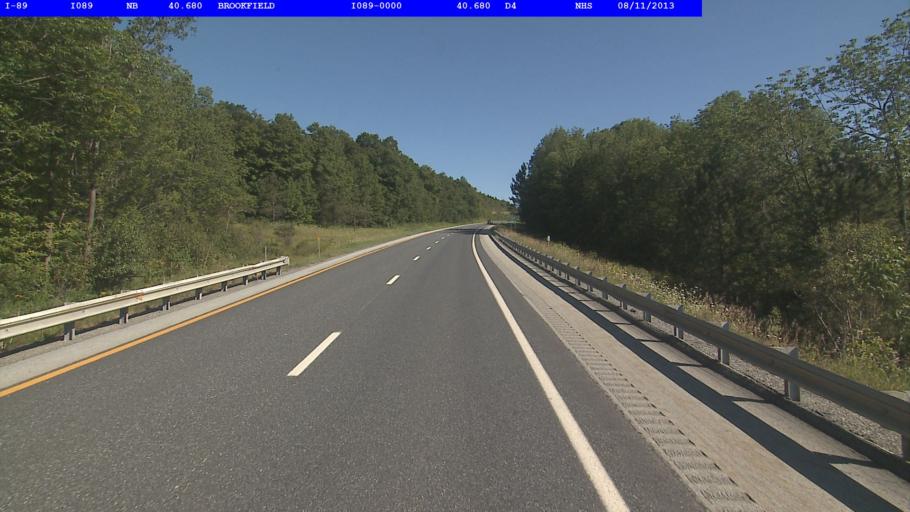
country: US
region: Vermont
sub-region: Washington County
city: Northfield
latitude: 44.0830
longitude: -72.6136
